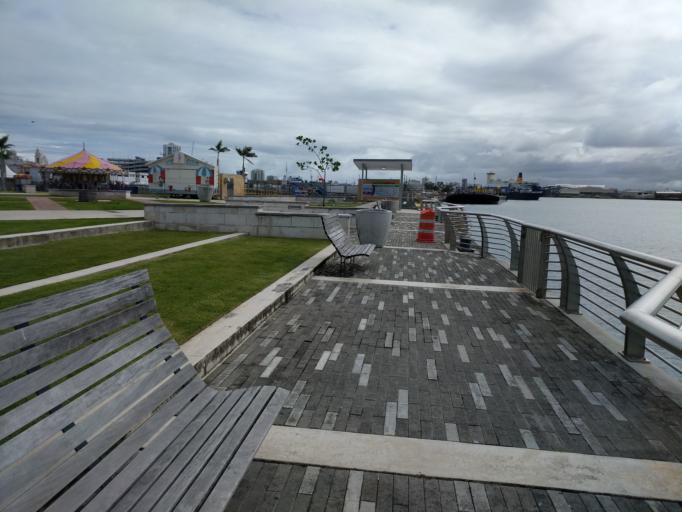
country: PR
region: San Juan
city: San Juan
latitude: 18.4633
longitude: -66.1061
